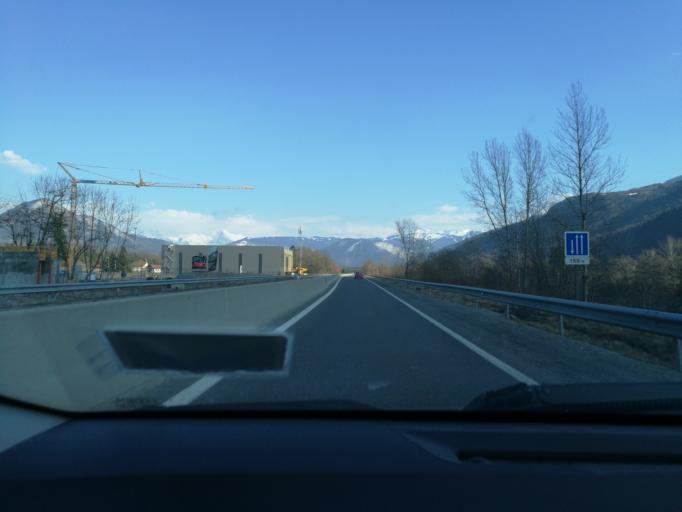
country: FR
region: Rhone-Alpes
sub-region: Departement de la Haute-Savoie
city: Ayse
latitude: 46.0733
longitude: 6.4607
